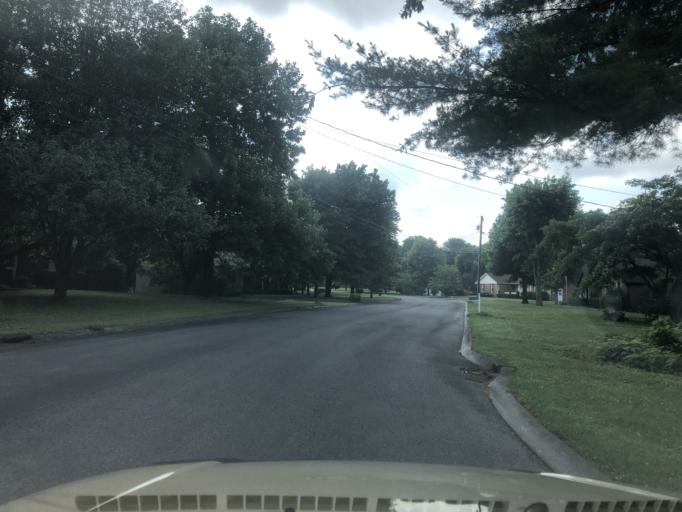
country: US
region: Tennessee
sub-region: Davidson County
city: Lakewood
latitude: 36.2311
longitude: -86.5934
